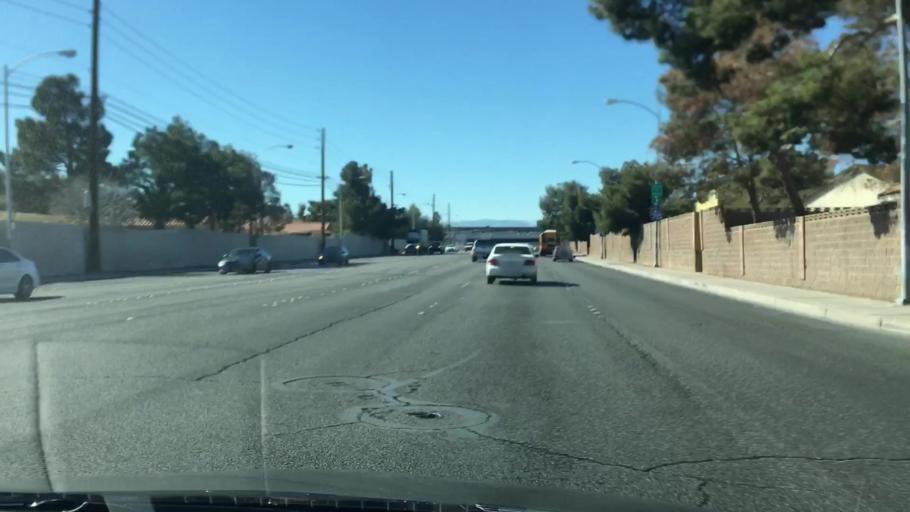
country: US
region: Nevada
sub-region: Clark County
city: Paradise
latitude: 36.0576
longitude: -115.1346
